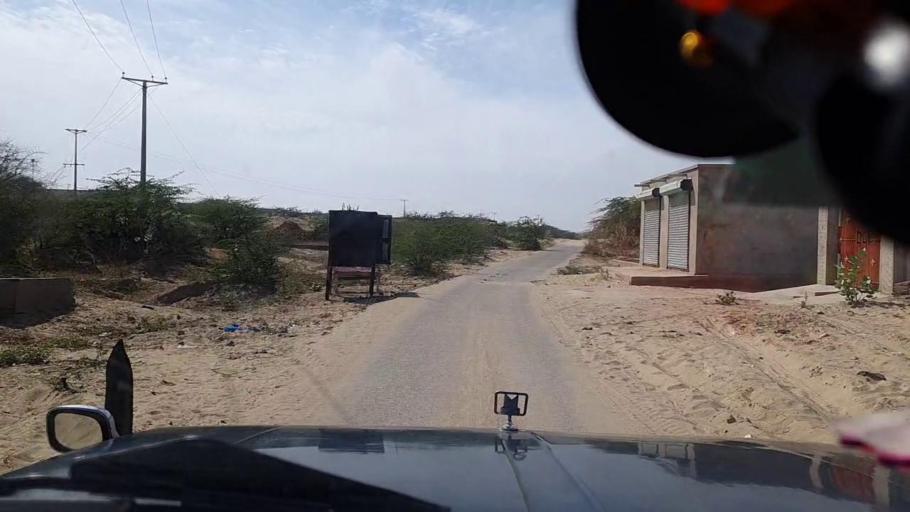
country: PK
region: Sindh
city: Diplo
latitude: 24.4583
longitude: 69.5796
